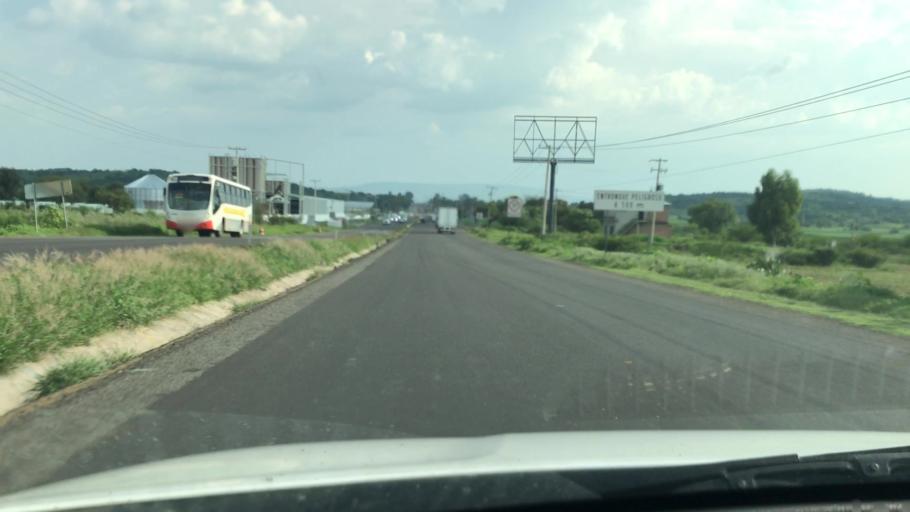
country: MX
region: Guanajuato
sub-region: Irapuato
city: San Ignacio de Rivera (Ojo de Agua)
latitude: 20.5574
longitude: -101.4504
